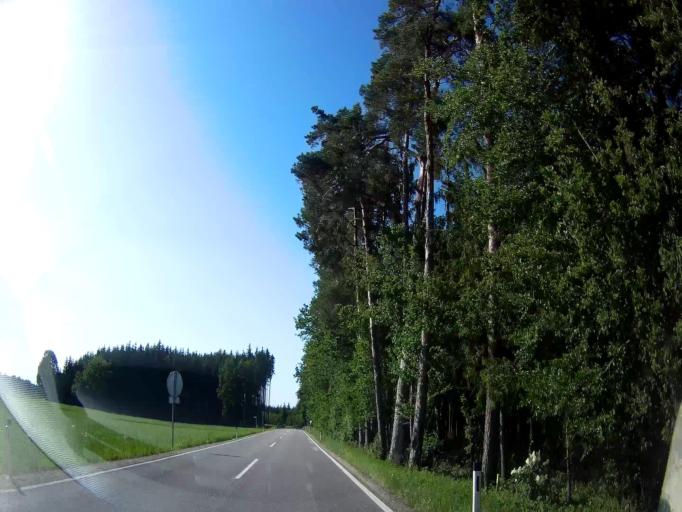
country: AT
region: Upper Austria
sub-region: Politischer Bezirk Braunau am Inn
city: Braunau am Inn
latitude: 48.1997
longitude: 13.0436
